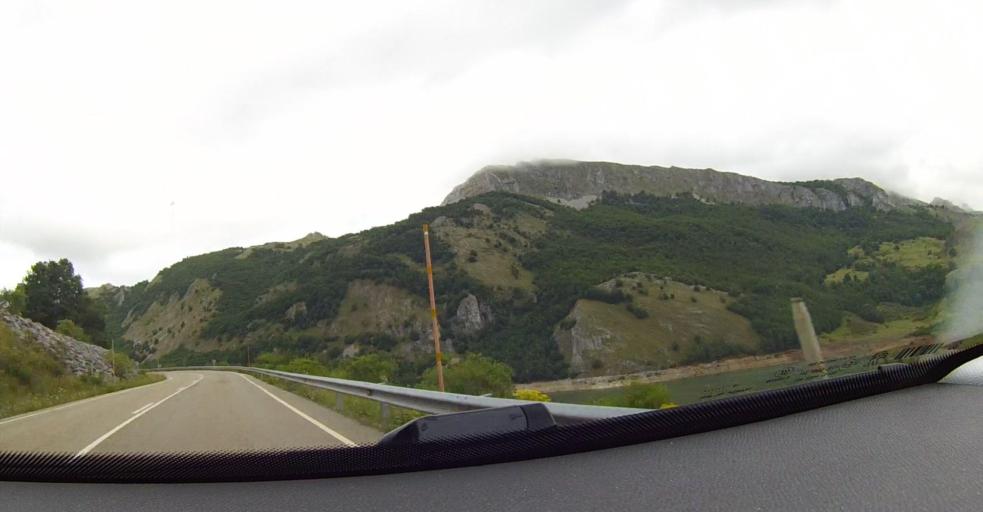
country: ES
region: Castille and Leon
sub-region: Provincia de Leon
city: Buron
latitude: 43.0168
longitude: -5.0333
